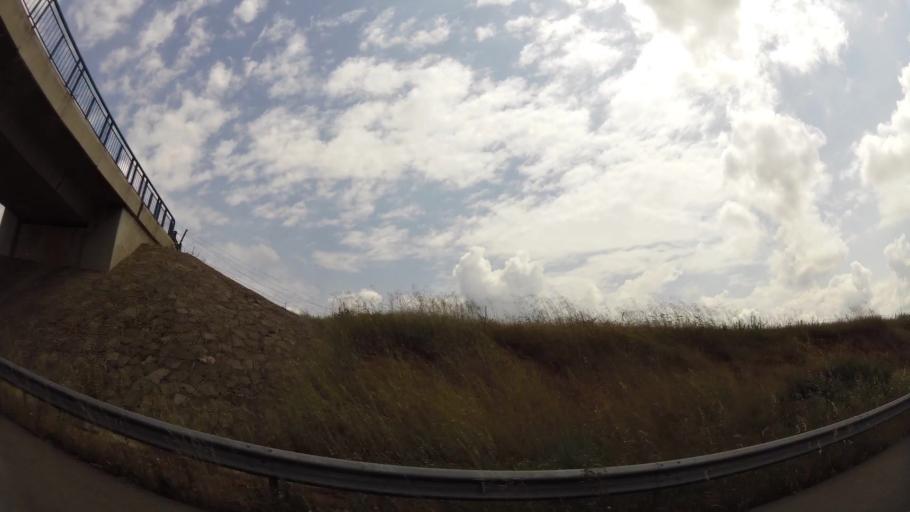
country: MA
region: Rabat-Sale-Zemmour-Zaer
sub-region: Khemisset
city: Tiflet
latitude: 33.9933
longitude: -6.5397
